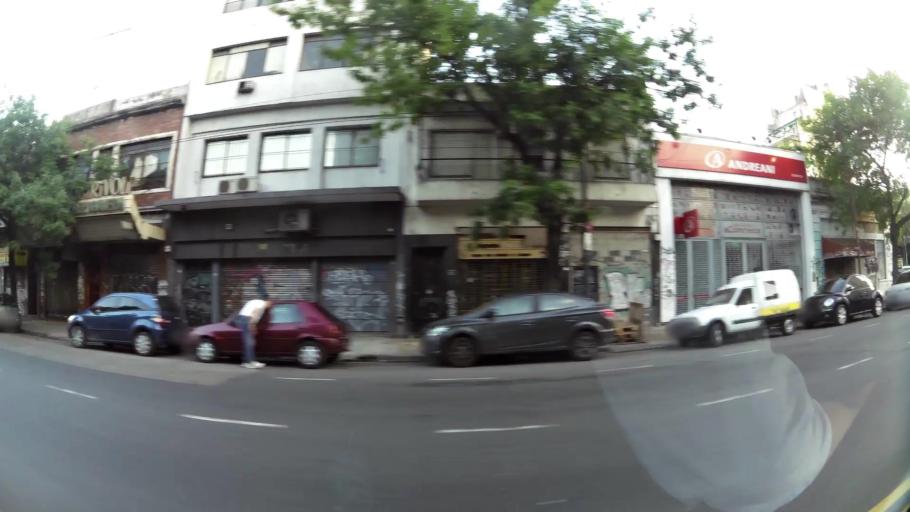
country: AR
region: Buenos Aires F.D.
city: Colegiales
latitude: -34.5976
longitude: -58.4353
